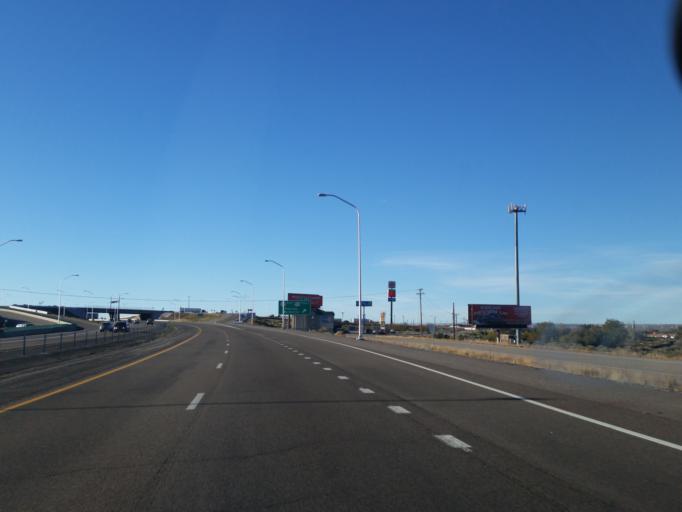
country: US
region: New Mexico
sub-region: Sandoval County
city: Bernalillo
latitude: 35.3213
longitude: -106.5318
